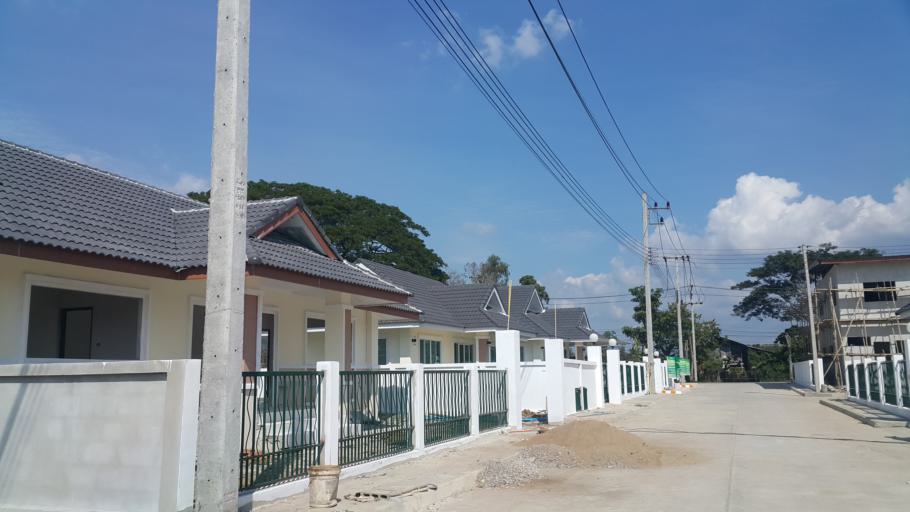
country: TH
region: Chiang Mai
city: San Kamphaeng
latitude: 18.7189
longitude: 99.1213
